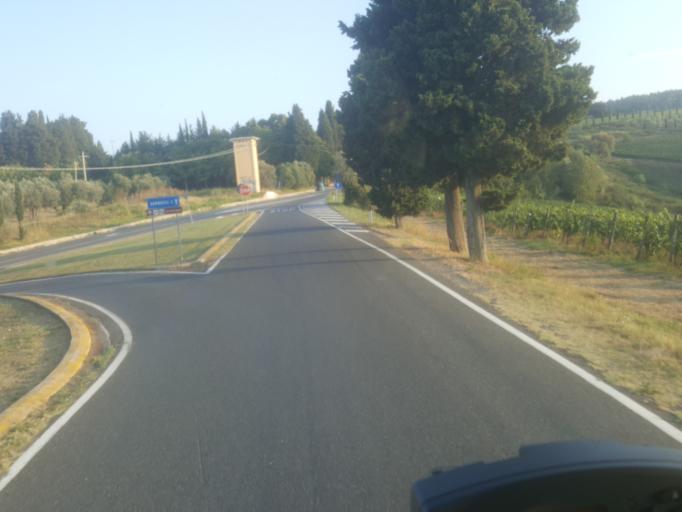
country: IT
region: Tuscany
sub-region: Province of Florence
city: Montaione
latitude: 43.5434
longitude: 10.9271
